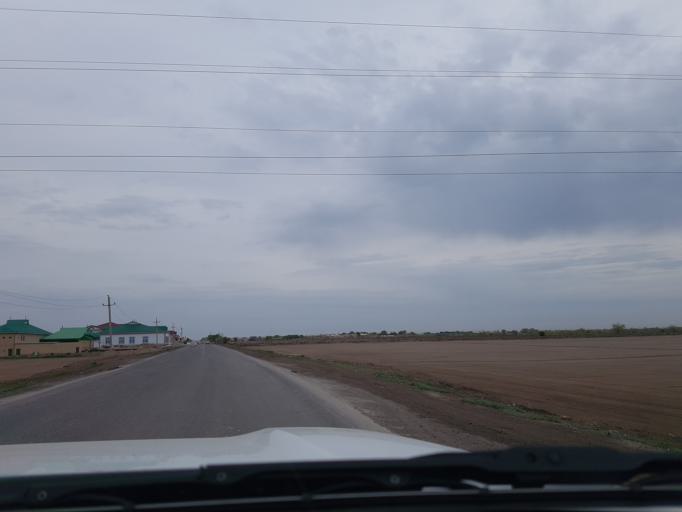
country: TM
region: Lebap
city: Turkmenabat
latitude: 39.0660
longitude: 63.5577
